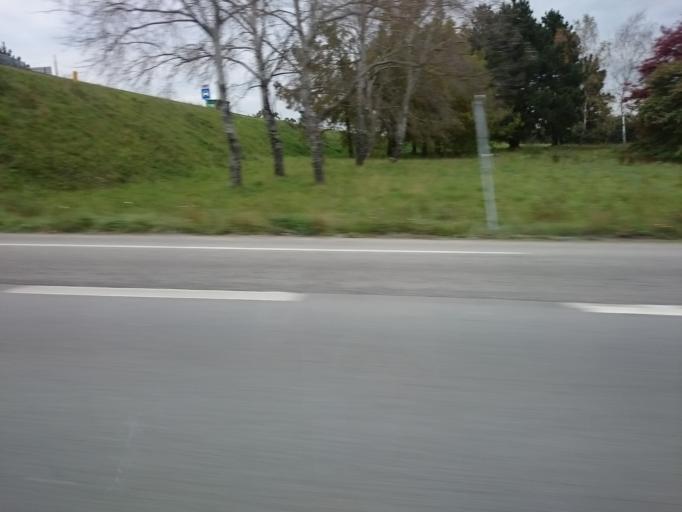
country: FR
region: Brittany
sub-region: Departement du Morbihan
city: Vannes
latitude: 47.6659
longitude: -2.7256
